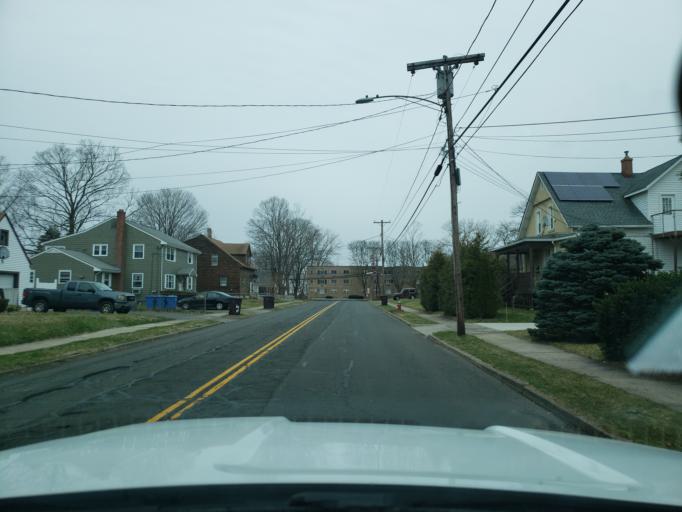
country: US
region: Connecticut
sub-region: Hartford County
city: New Britain
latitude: 41.6881
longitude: -72.7908
